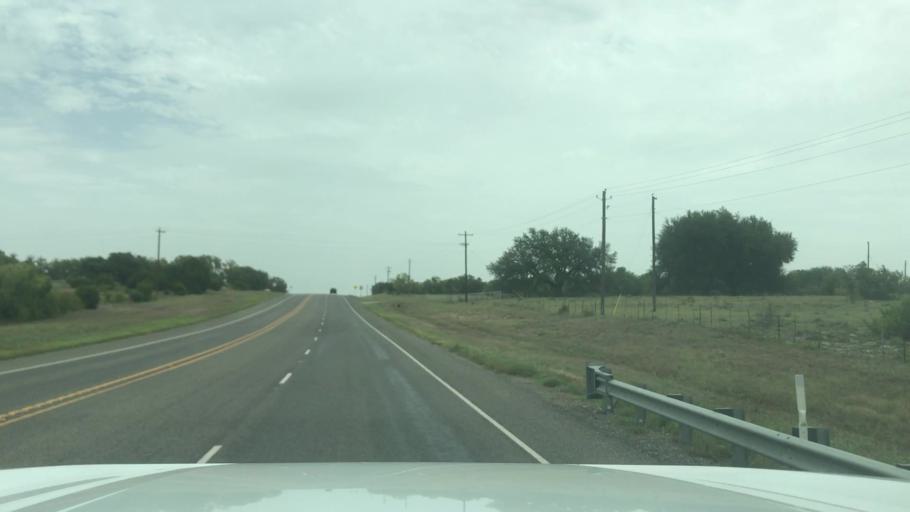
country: US
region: Texas
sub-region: Hamilton County
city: Hico
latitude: 31.9806
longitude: -98.0195
